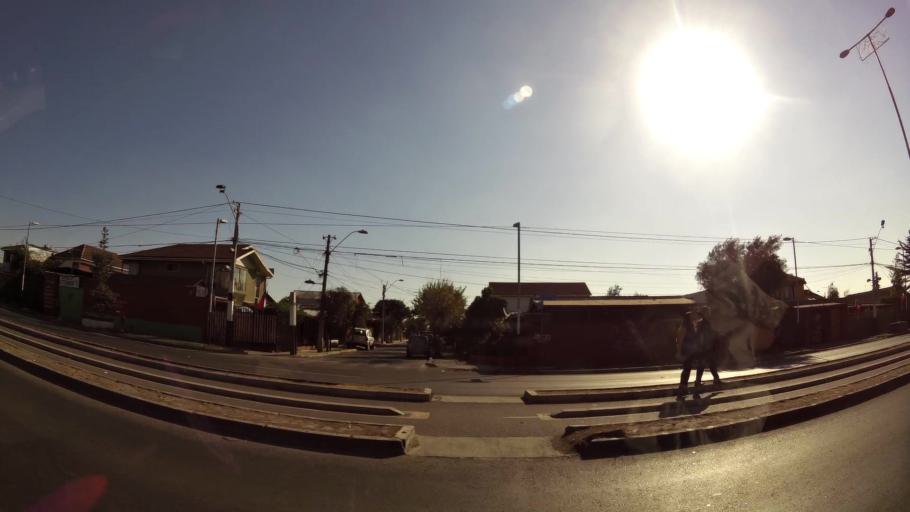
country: CL
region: Santiago Metropolitan
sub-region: Provincia de Santiago
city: La Pintana
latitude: -33.5543
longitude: -70.6168
